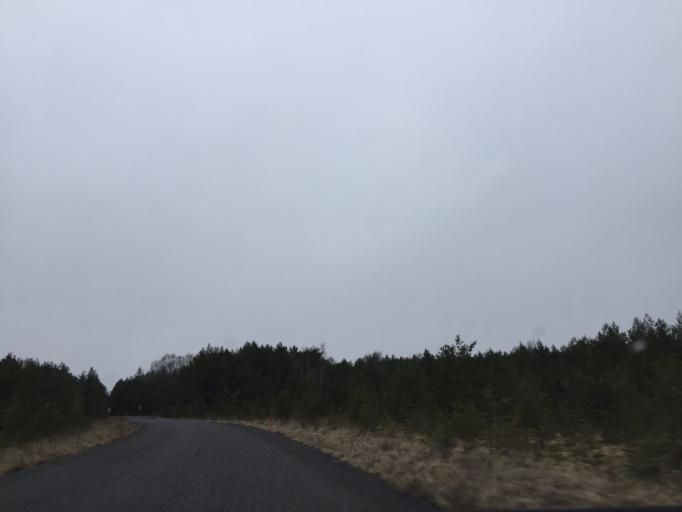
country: EE
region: Laeaene
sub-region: Ridala Parish
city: Uuemoisa
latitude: 58.6723
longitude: 23.5610
